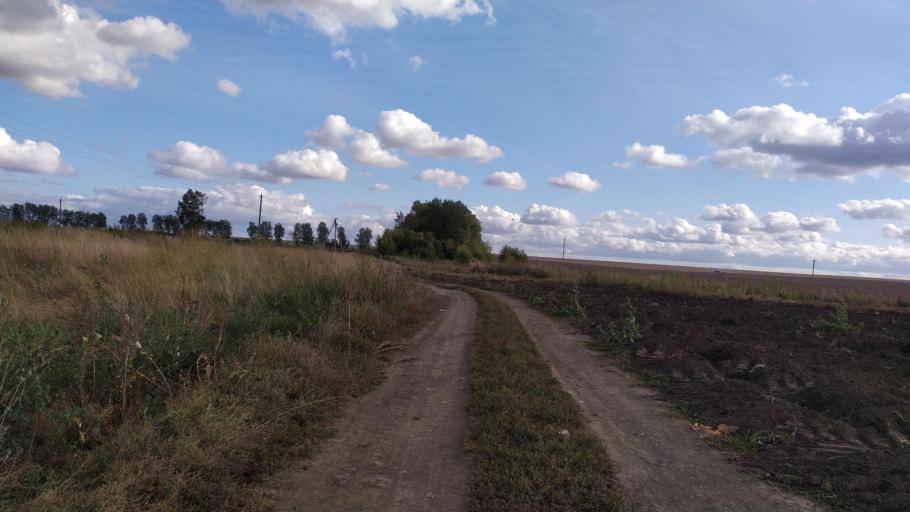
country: RU
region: Kursk
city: Kursk
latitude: 51.6262
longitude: 36.1596
